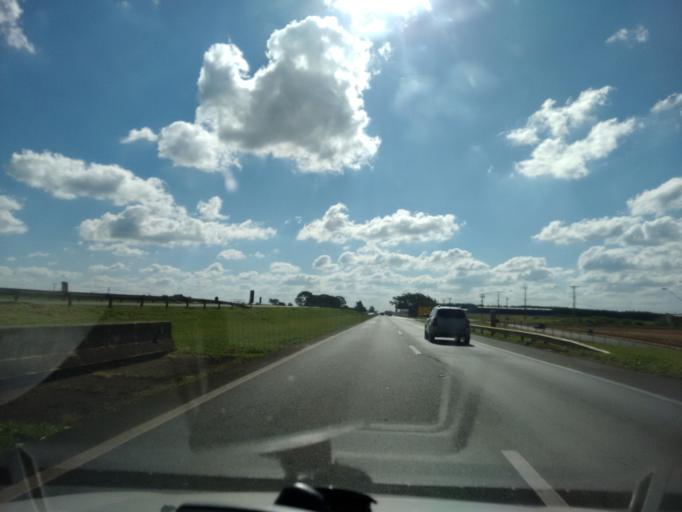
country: BR
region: Sao Paulo
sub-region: Ibate
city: Ibate
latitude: -21.9409
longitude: -48.0061
